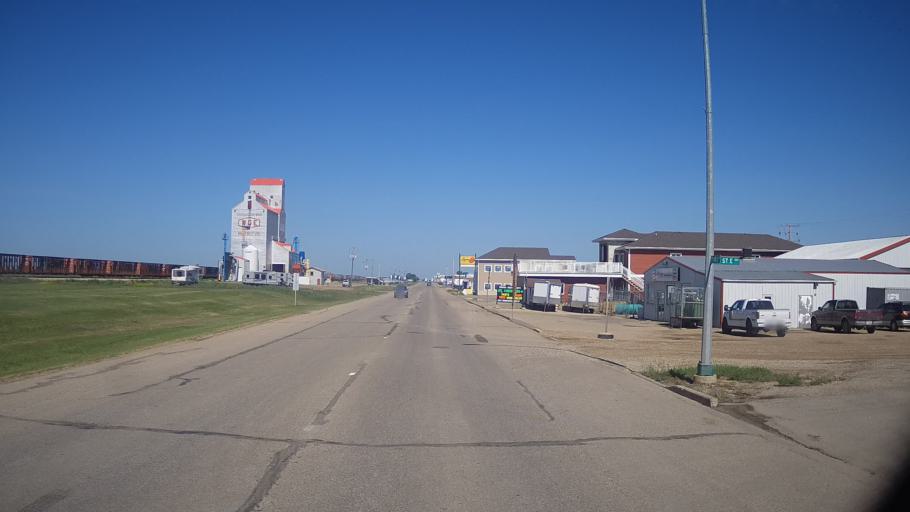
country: CA
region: Saskatchewan
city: Watrous
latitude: 51.6673
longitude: -105.4557
